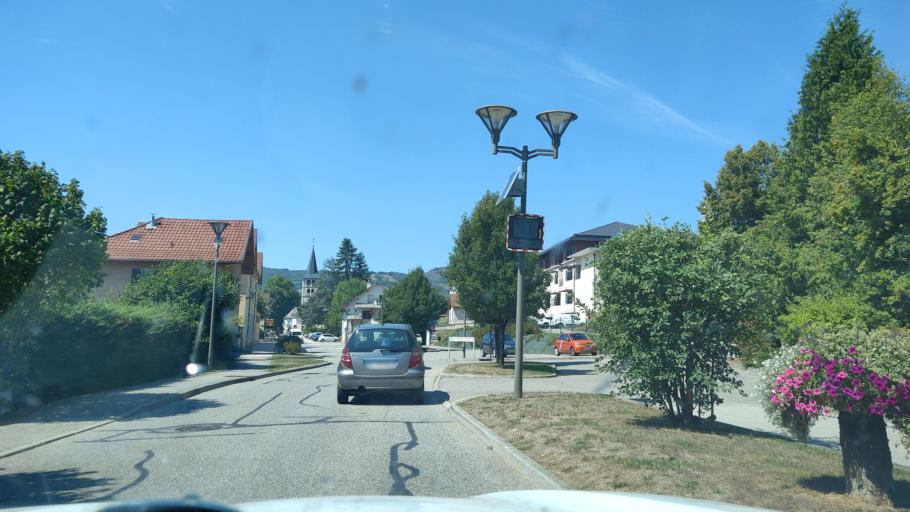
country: FR
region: Rhone-Alpes
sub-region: Departement de la Savoie
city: Novalaise
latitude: 45.5944
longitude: 5.7744
